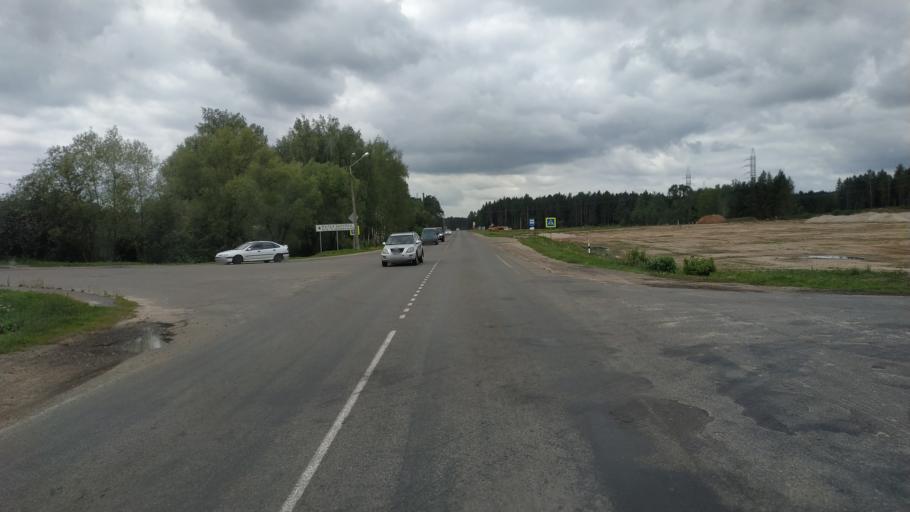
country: BY
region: Mogilev
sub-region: Mahilyowski Rayon
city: Veyno
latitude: 53.8752
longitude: 30.4319
